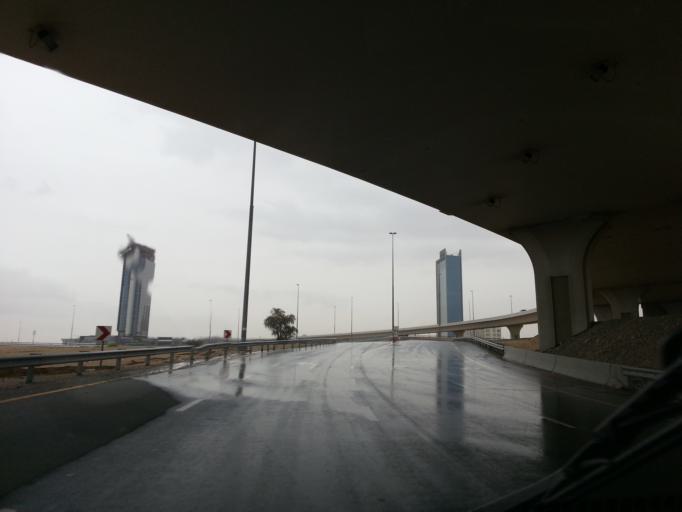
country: AE
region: Dubai
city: Dubai
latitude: 25.0506
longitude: 55.2219
